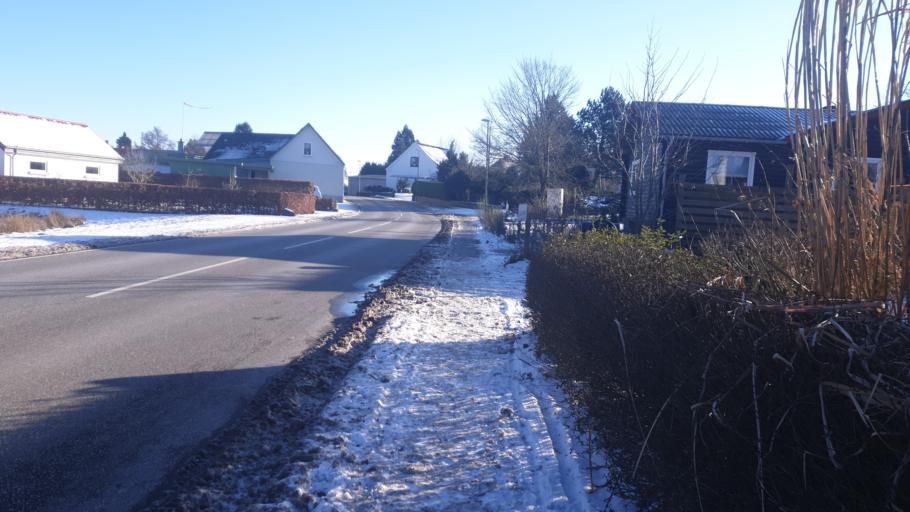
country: DK
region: Central Jutland
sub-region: Hedensted Kommune
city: Hedensted
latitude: 55.7810
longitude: 9.7123
